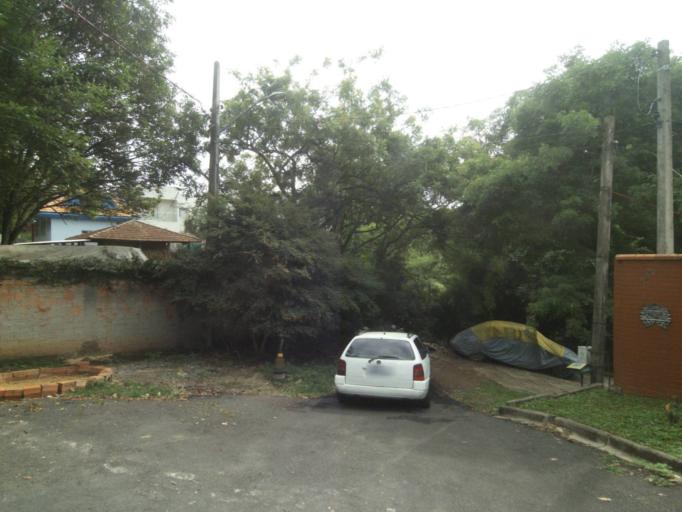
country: BR
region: Parana
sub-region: Curitiba
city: Curitiba
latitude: -25.4053
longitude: -49.2955
